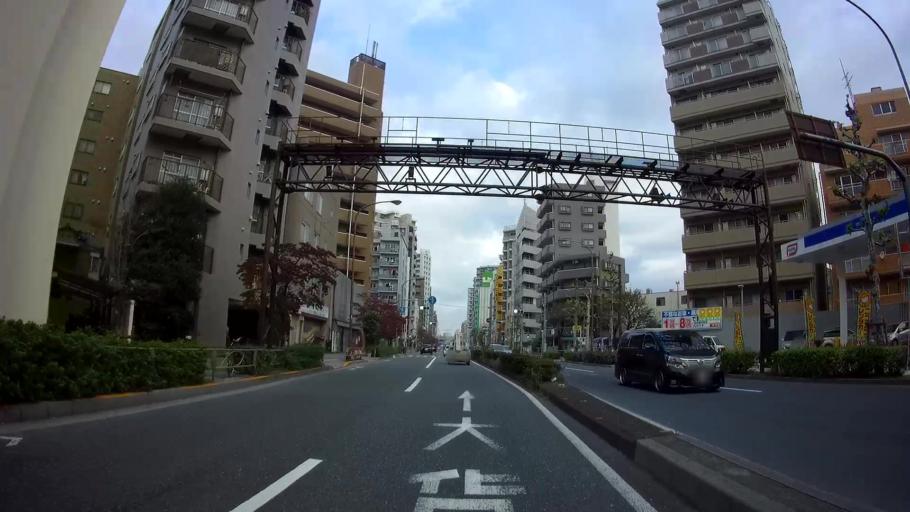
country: JP
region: Tokyo
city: Tokyo
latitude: 35.7452
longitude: 139.7017
